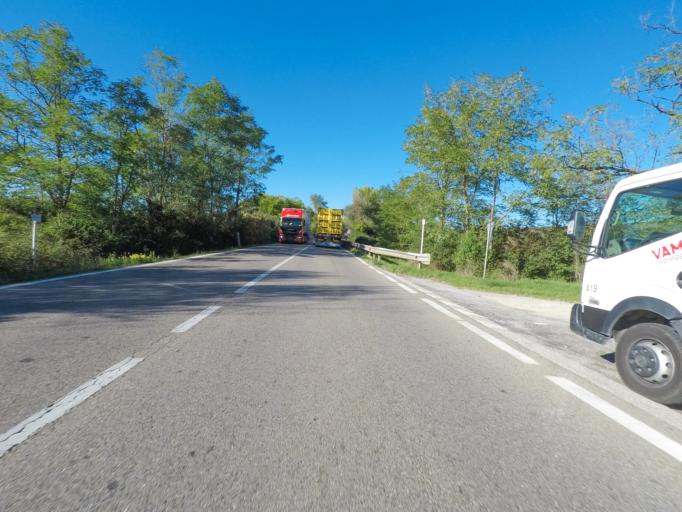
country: IT
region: Tuscany
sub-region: Provincia di Siena
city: Rosia
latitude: 43.1988
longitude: 11.2762
